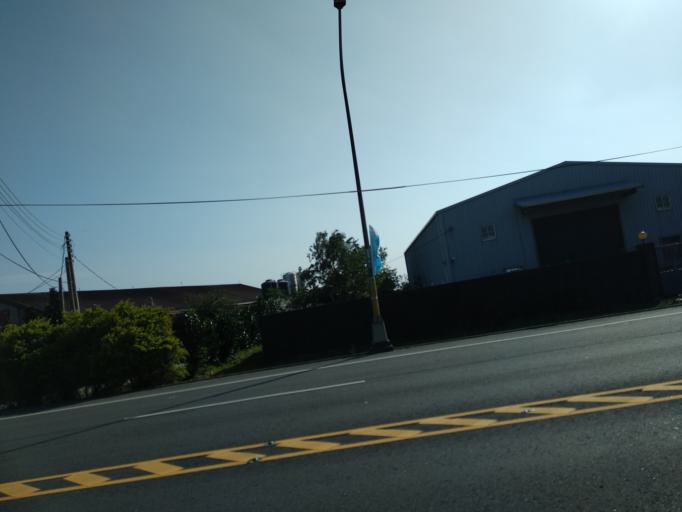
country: TW
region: Taiwan
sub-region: Hsinchu
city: Zhubei
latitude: 24.9840
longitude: 121.0563
